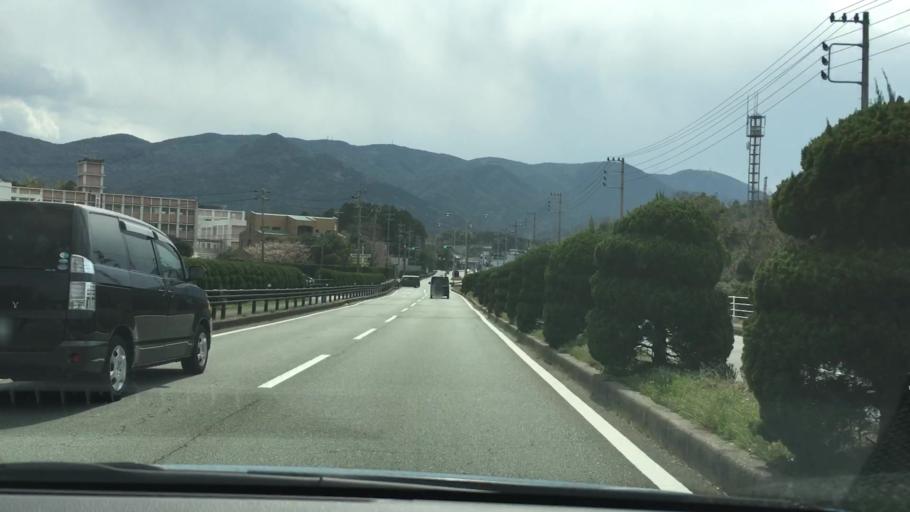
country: JP
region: Mie
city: Toba
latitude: 34.4844
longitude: 136.8259
